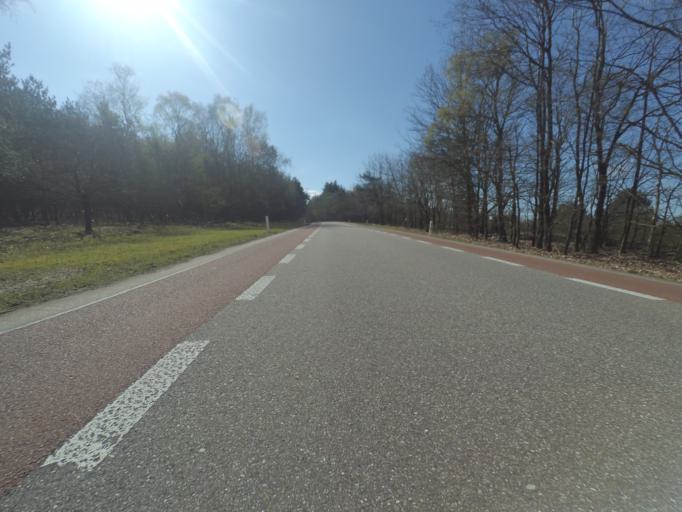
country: NL
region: Gelderland
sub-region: Gemeente Arnhem
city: Hoogkamp
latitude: 52.0734
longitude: 5.8812
